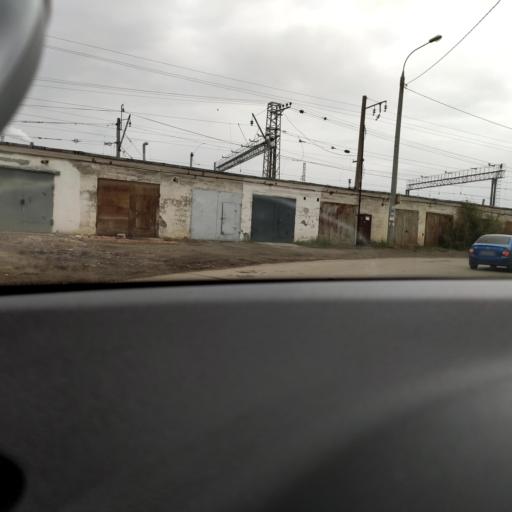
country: RU
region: Samara
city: Samara
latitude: 53.1786
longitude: 50.1450
